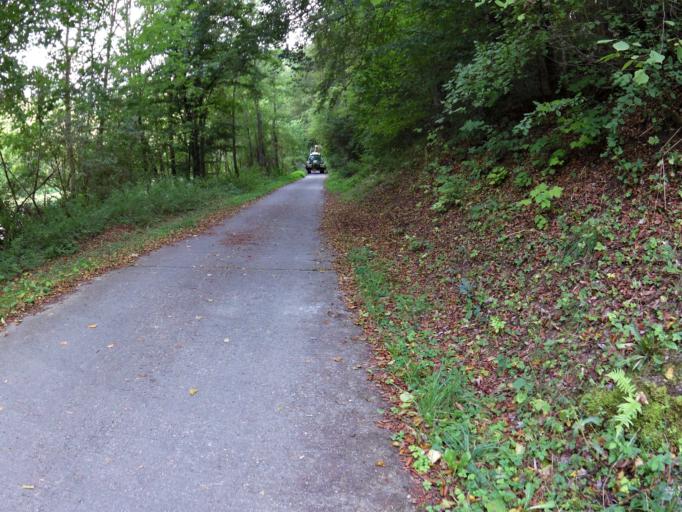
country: DE
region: Baden-Wuerttemberg
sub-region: Freiburg Region
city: Villingendorf
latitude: 48.2064
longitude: 8.6059
